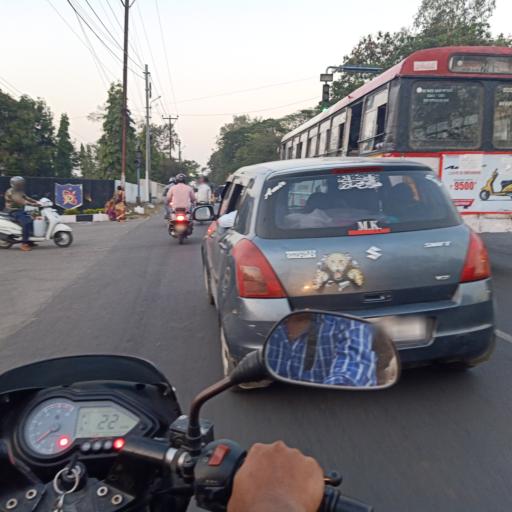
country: IN
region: Telangana
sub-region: Rangareddi
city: Secunderabad
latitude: 17.4846
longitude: 78.5114
